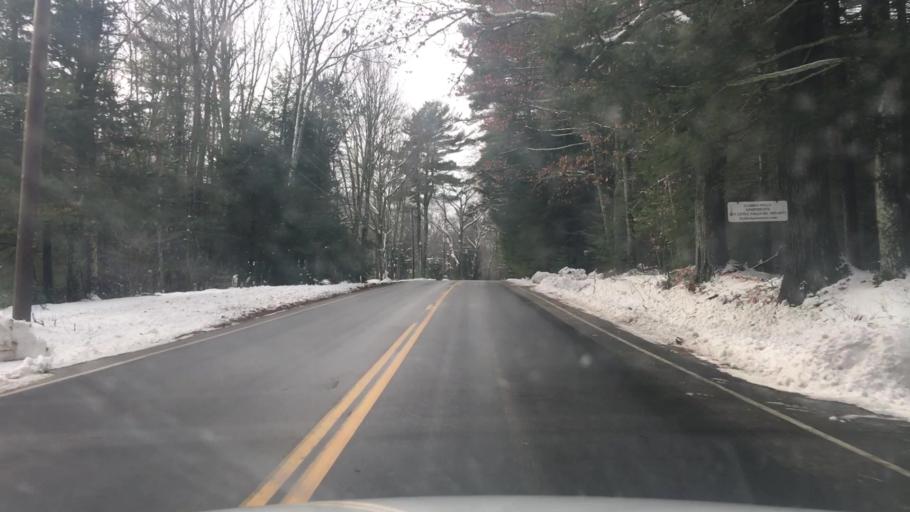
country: US
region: Maine
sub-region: York County
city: Hollis Center
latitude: 43.5827
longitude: -70.5969
